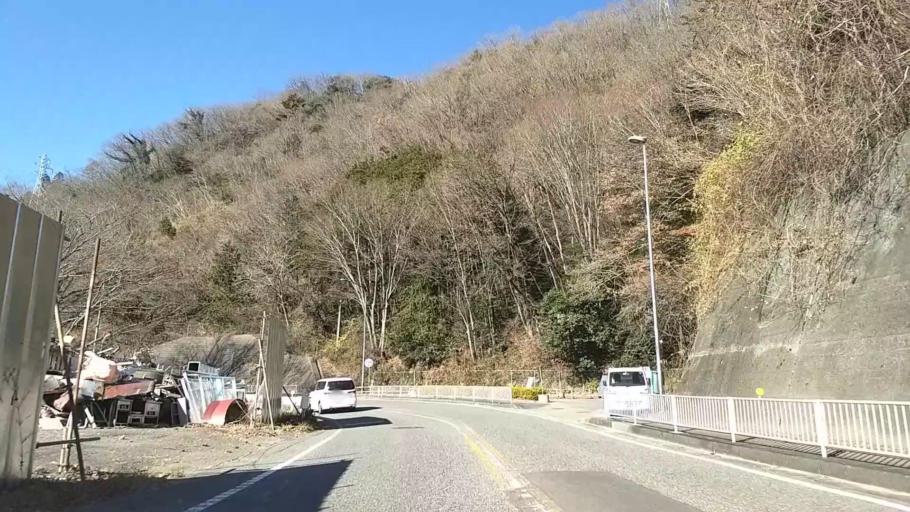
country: JP
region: Yamanashi
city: Uenohara
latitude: 35.6175
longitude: 139.0971
